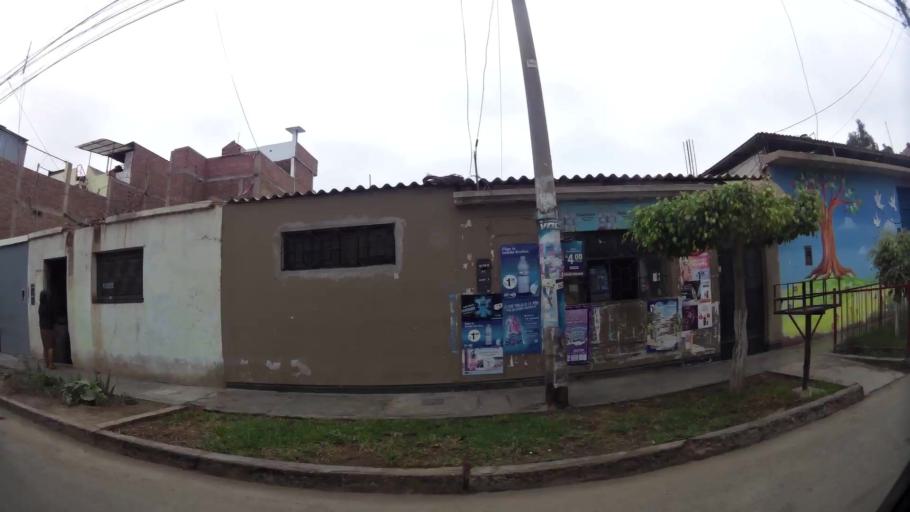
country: PE
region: La Libertad
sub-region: Provincia de Trujillo
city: La Esperanza
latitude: -8.0986
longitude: -79.0453
